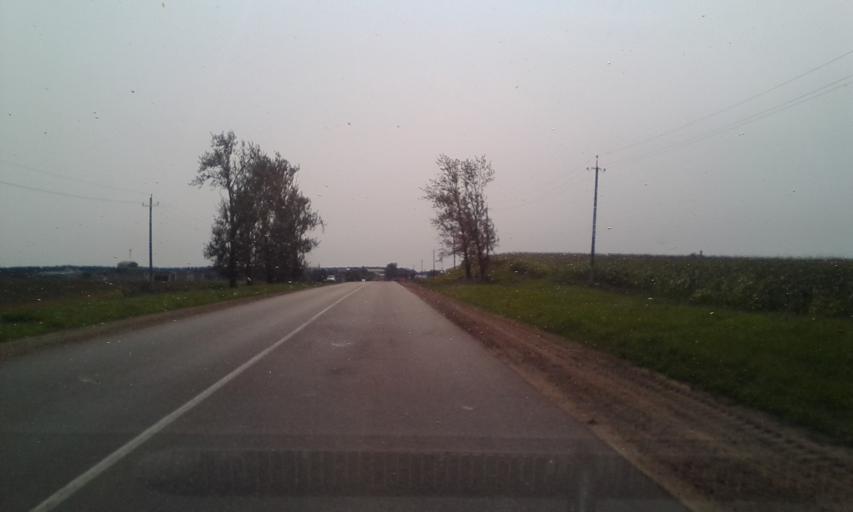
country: BY
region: Minsk
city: Hatava
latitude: 53.7895
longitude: 27.6511
